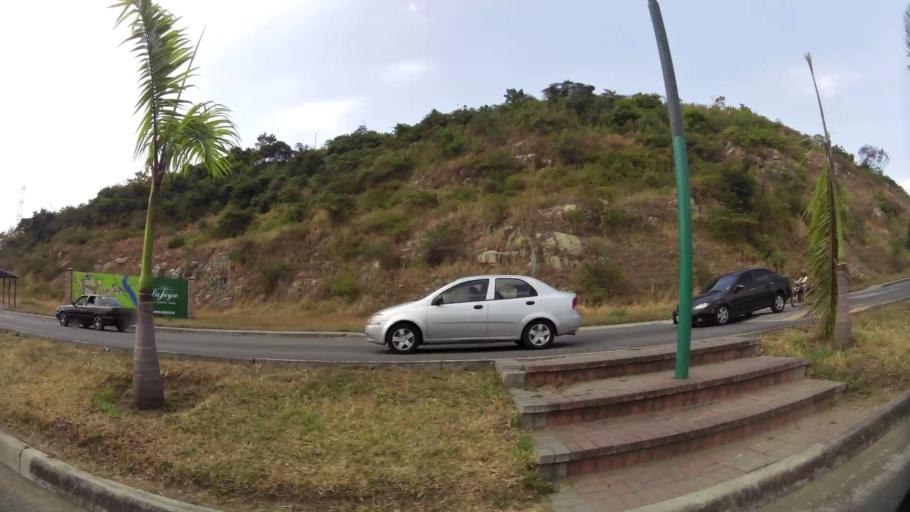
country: EC
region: Guayas
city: El Triunfo
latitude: -2.0387
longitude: -79.9153
